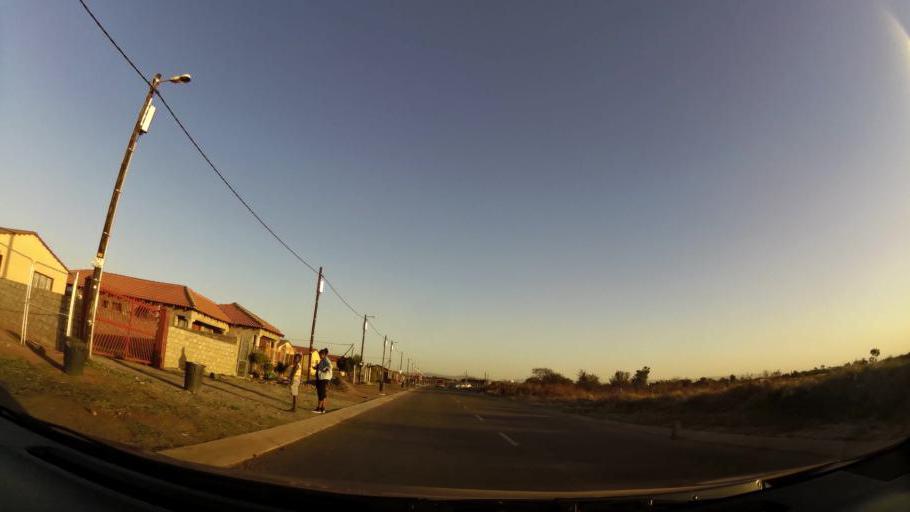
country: ZA
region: North-West
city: Ga-Rankuwa
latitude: -25.6029
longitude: 28.0974
